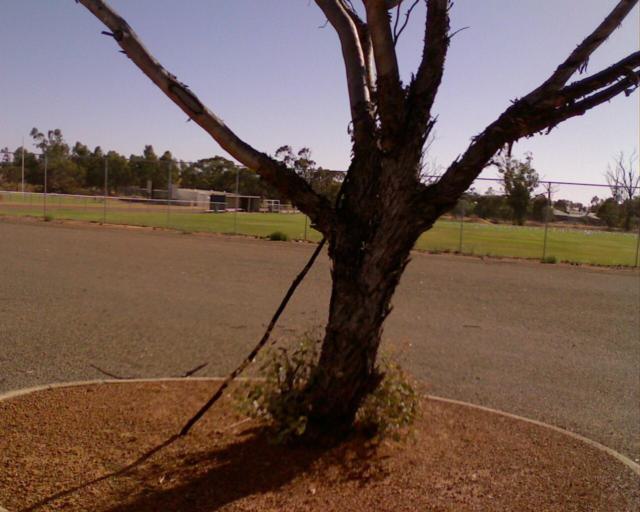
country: AU
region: Western Australia
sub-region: Wongan-Ballidu
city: Wongan Hills
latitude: -30.2752
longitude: 116.6569
